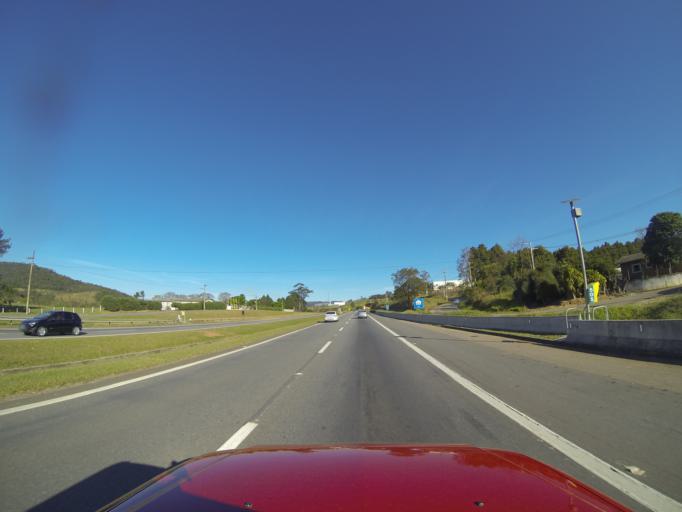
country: BR
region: Sao Paulo
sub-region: Bom Jesus Dos Perdoes
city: Bom Jesus dos Perdoes
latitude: -23.1633
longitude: -46.4467
